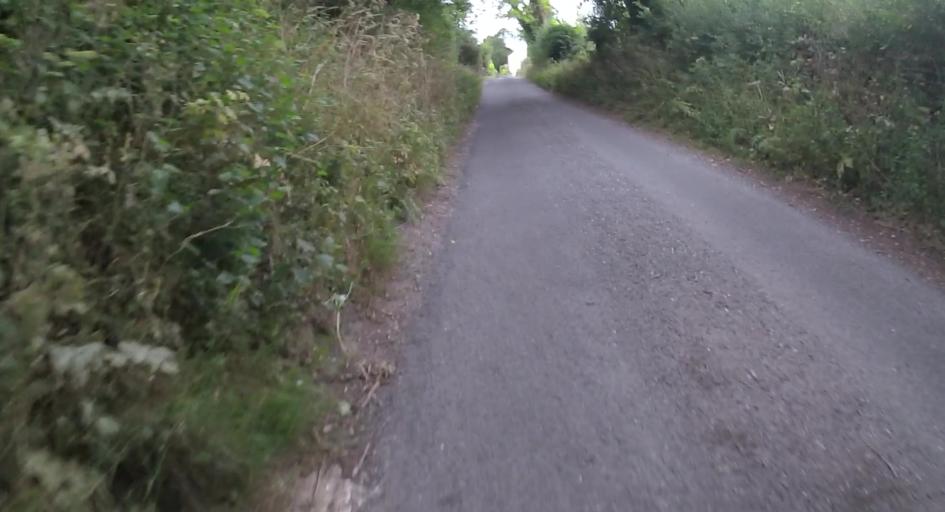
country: GB
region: England
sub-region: Hampshire
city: Basingstoke
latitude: 51.2064
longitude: -1.1659
